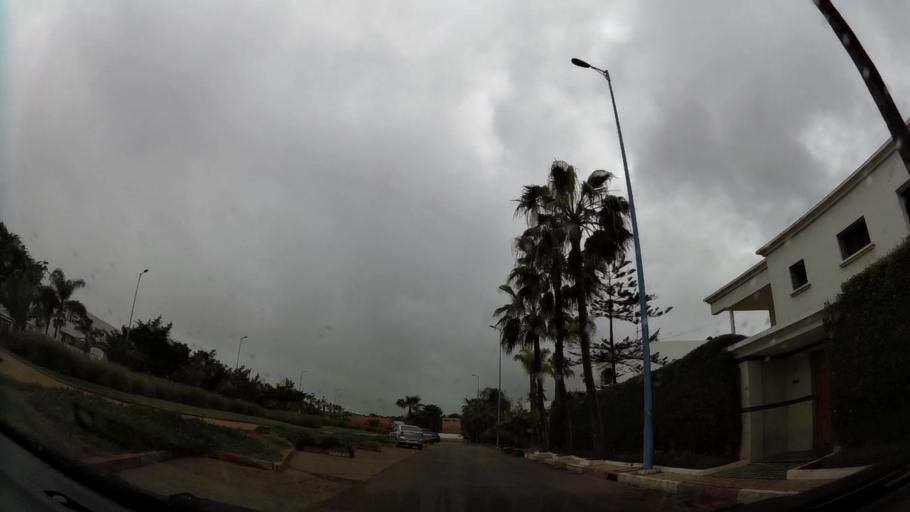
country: MA
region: Grand Casablanca
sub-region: Casablanca
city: Casablanca
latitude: 33.5379
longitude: -7.6292
